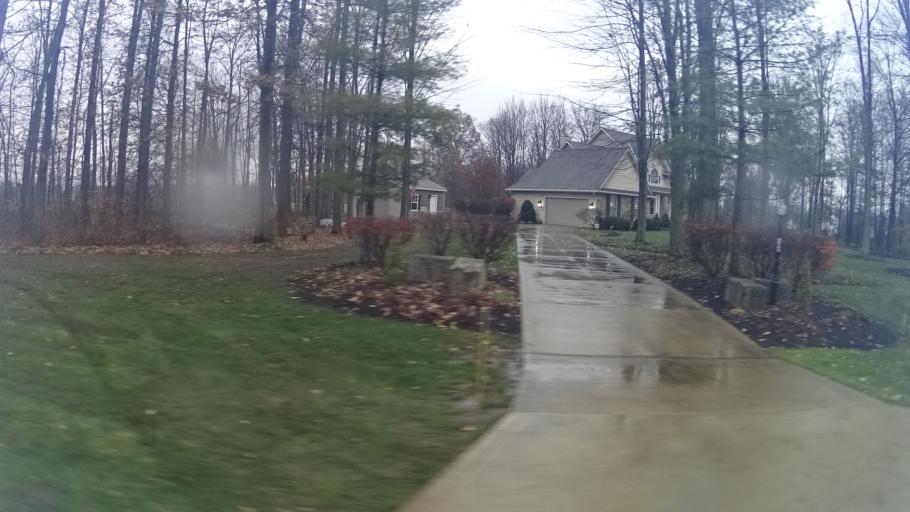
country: US
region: Ohio
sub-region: Lorain County
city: Lagrange
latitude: 41.2951
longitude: -82.1273
